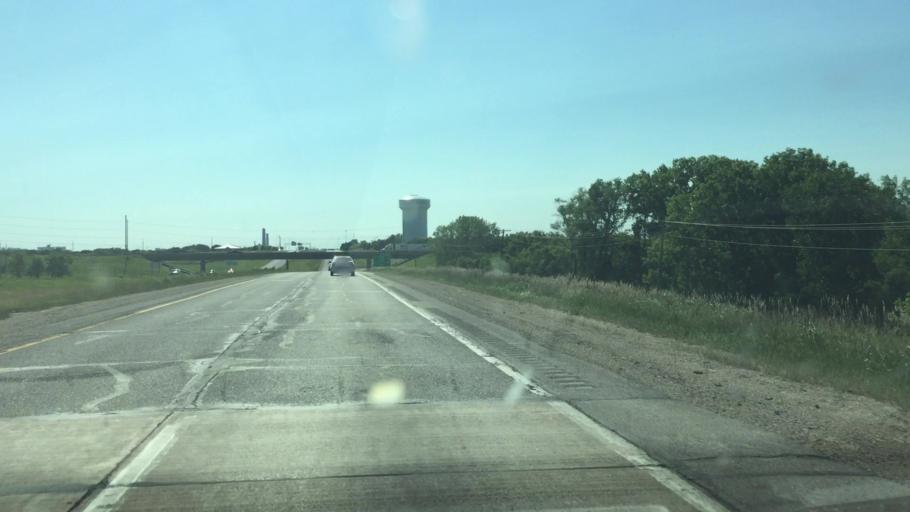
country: US
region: Iowa
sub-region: Linn County
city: Ely
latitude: 41.9267
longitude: -91.6331
